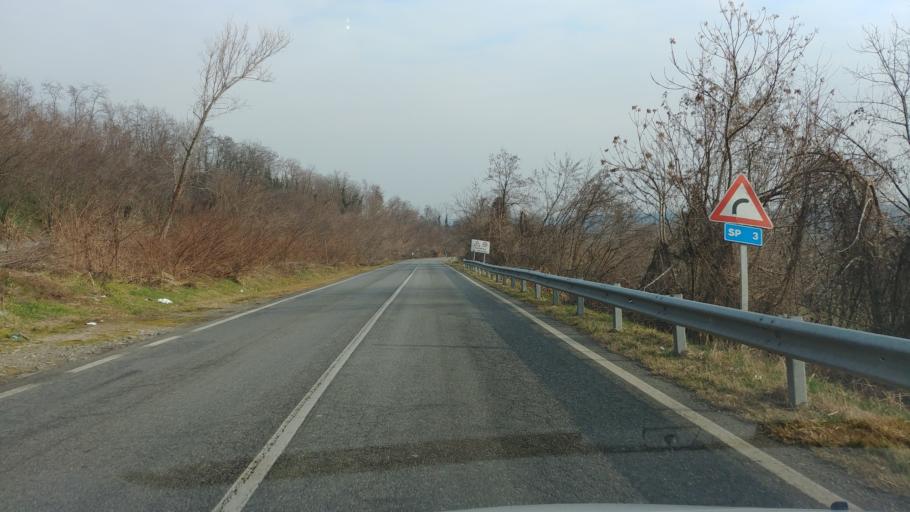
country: IT
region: Piedmont
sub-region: Provincia di Cuneo
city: Castelletto Stura
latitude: 44.4591
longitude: 7.6326
